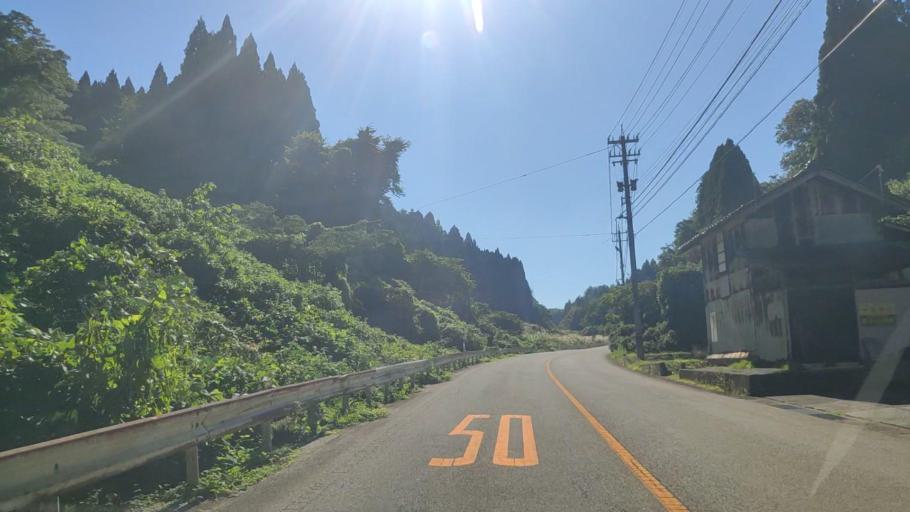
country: JP
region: Ishikawa
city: Nanao
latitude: 37.3218
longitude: 137.1784
